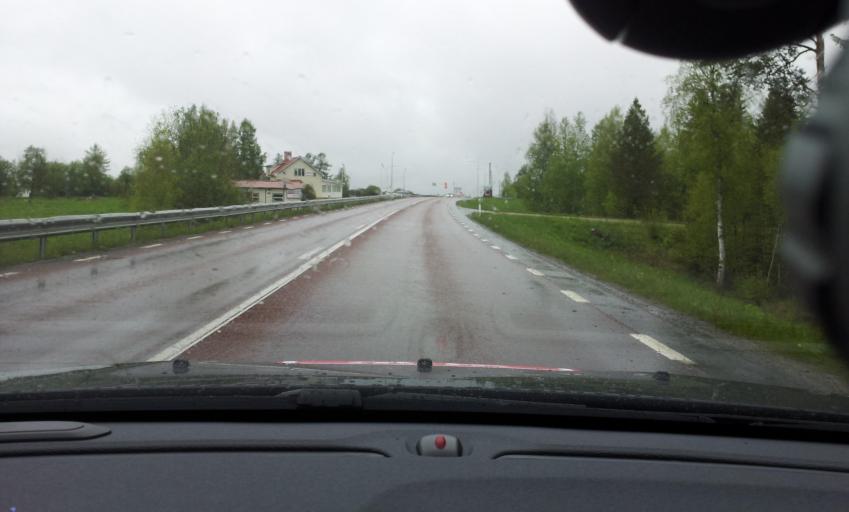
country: SE
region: Jaemtland
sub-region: Bergs Kommun
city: Hoverberg
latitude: 62.9076
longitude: 14.5226
